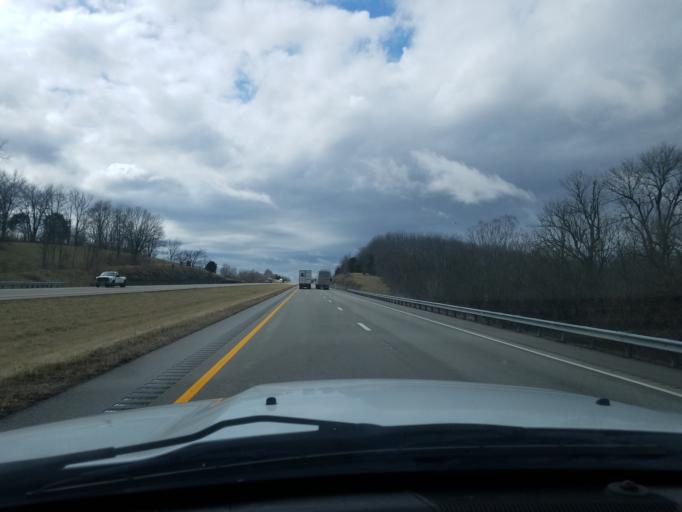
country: US
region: Kentucky
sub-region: Montgomery County
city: Mount Sterling
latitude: 38.0964
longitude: -83.8618
